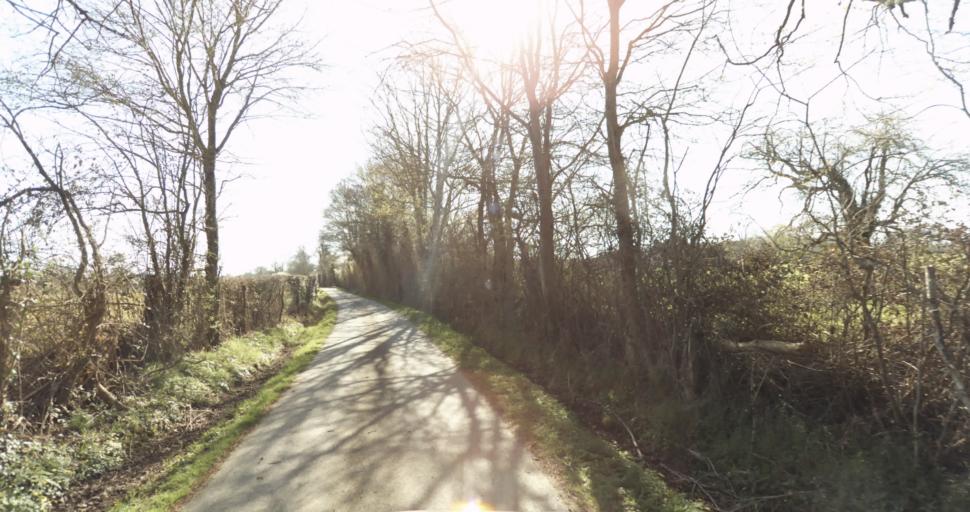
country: FR
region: Lower Normandy
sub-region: Departement du Calvados
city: Saint-Pierre-sur-Dives
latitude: 49.0527
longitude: 0.0569
